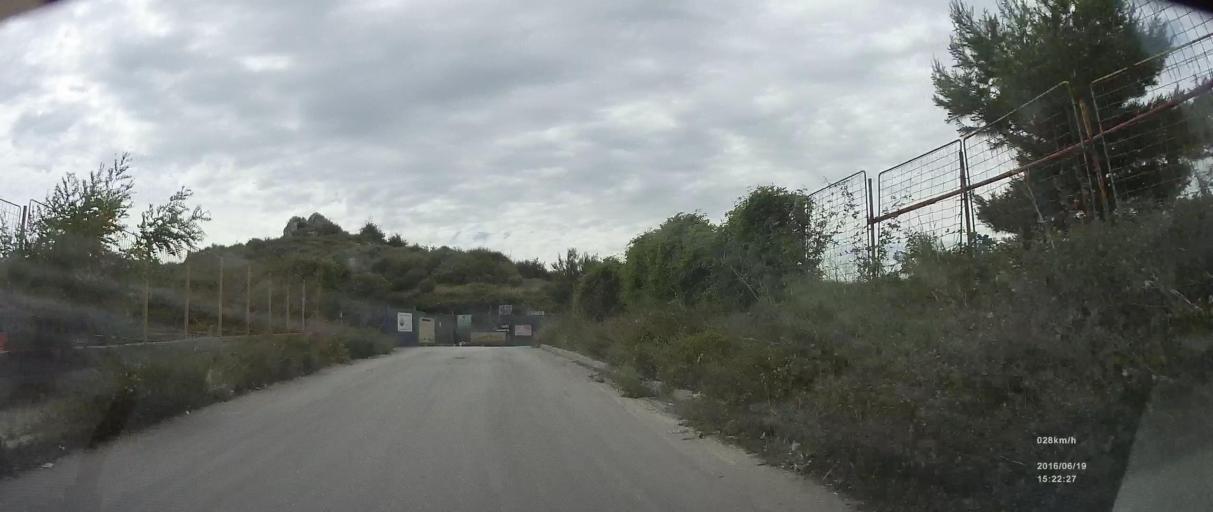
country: HR
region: Splitsko-Dalmatinska
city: Kamen
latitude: 43.5110
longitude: 16.5013
